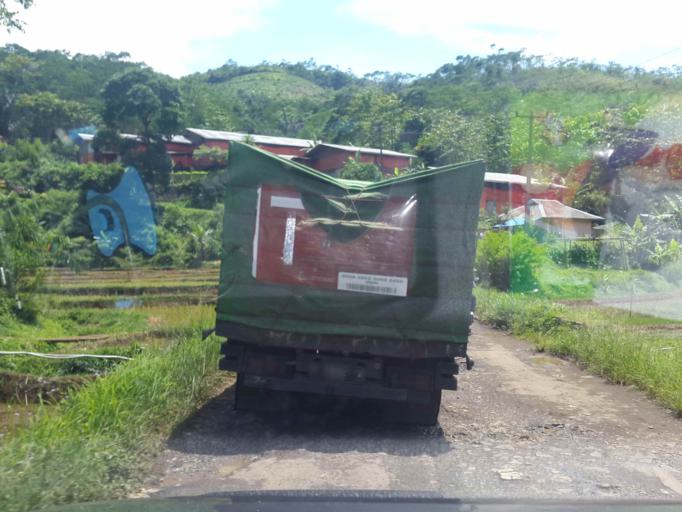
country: ID
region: West Java
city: Kupel
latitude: -7.0851
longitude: 107.1611
